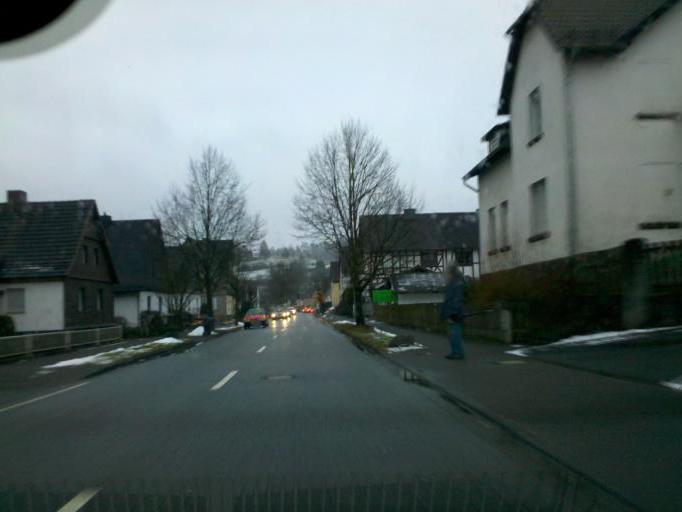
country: DE
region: Hesse
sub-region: Regierungsbezirk Giessen
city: Breidenbach
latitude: 50.8426
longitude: 8.4673
